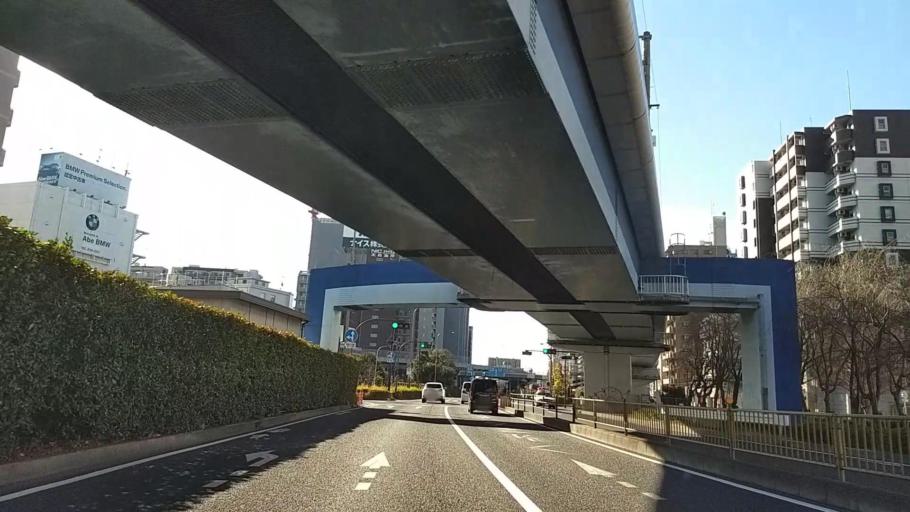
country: JP
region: Kanagawa
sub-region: Kawasaki-shi
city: Kawasaki
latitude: 35.5932
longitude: 139.7364
